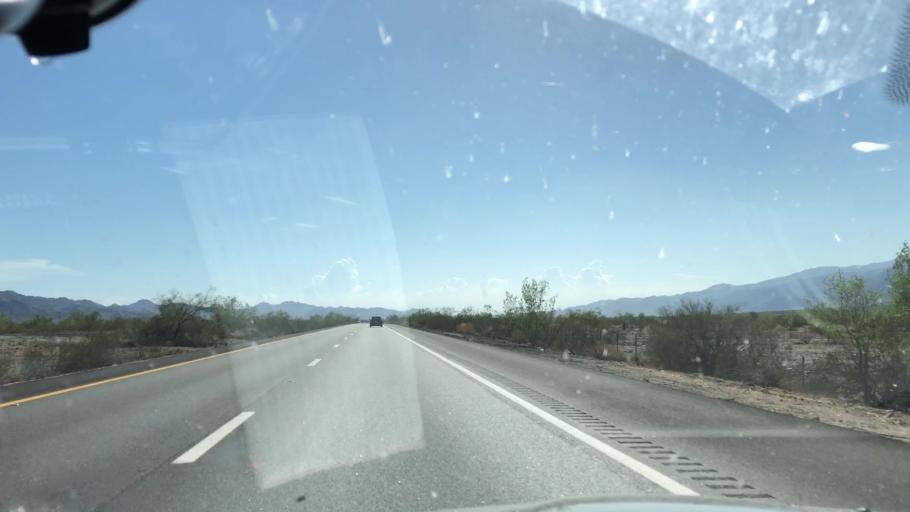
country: US
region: California
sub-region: Imperial County
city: Niland
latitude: 33.6863
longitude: -115.5259
